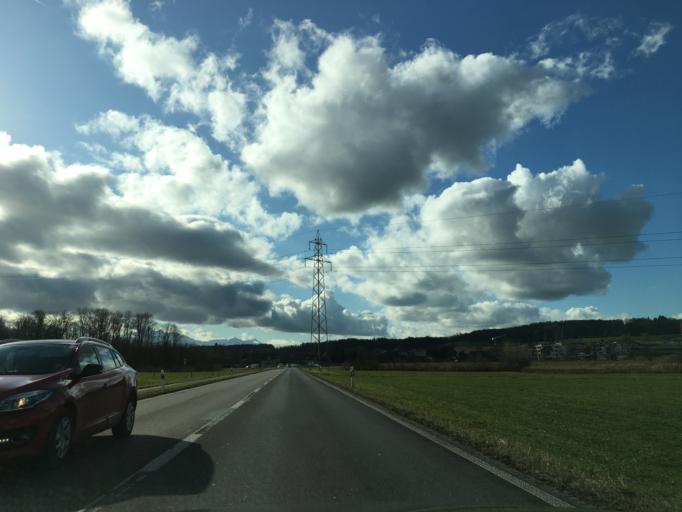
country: CH
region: Aargau
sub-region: Bezirk Muri
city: Sins
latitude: 47.1906
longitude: 8.4065
